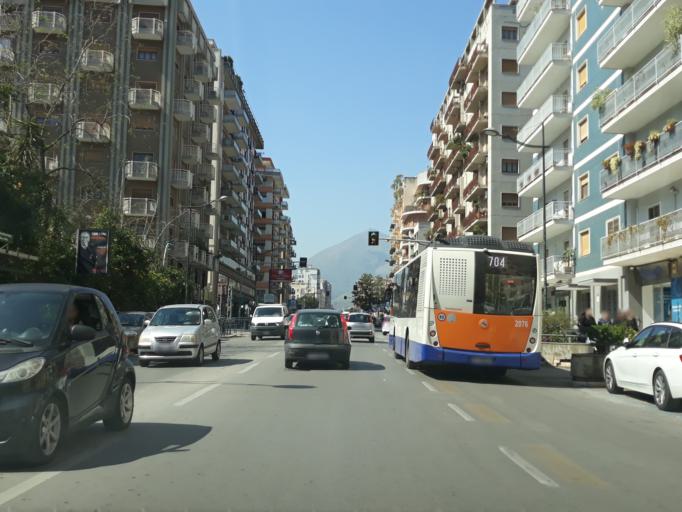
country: IT
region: Sicily
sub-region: Palermo
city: Palermo
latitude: 38.1326
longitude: 13.3451
